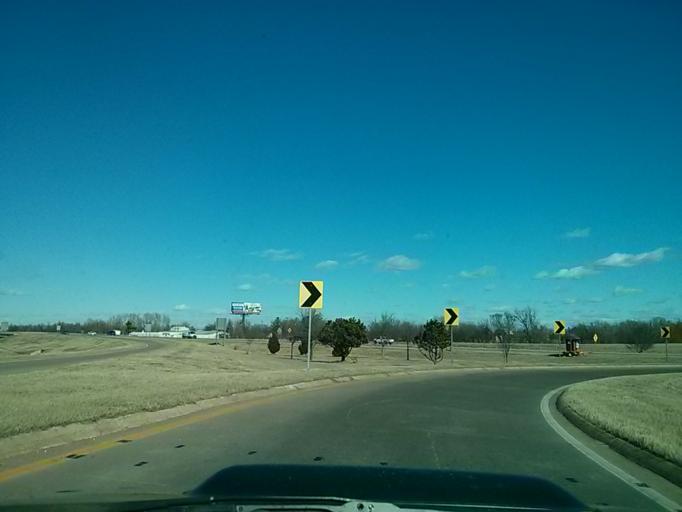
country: US
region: Oklahoma
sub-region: Tulsa County
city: Turley
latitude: 36.2077
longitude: -95.9477
